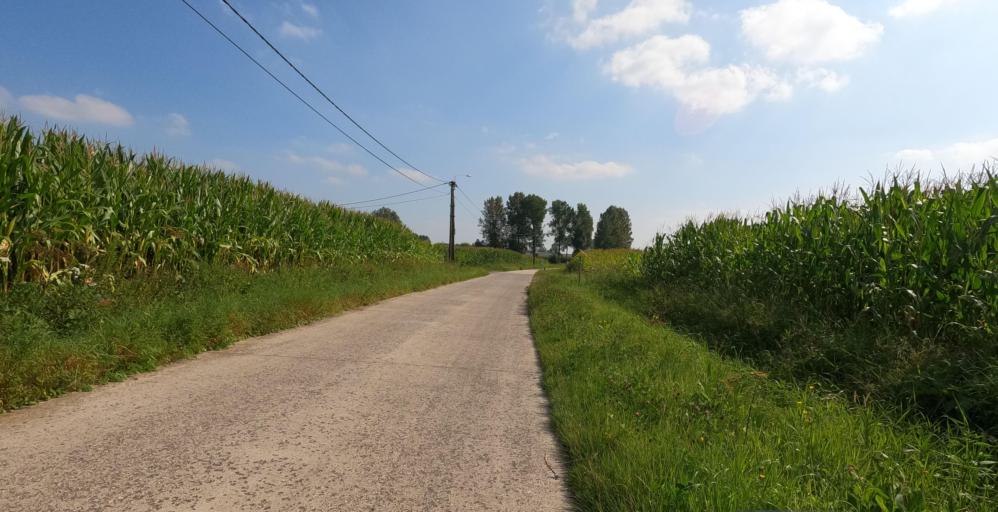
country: BE
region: Flanders
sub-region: Provincie Oost-Vlaanderen
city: Beveren
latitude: 51.1637
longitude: 4.2494
